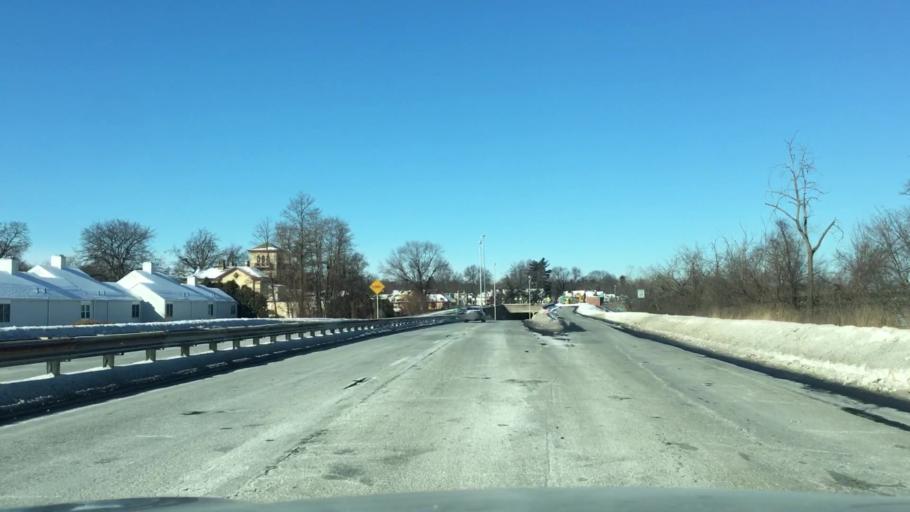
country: US
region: Massachusetts
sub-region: Hampden County
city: West Springfield
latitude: 42.1054
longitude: -72.6128
